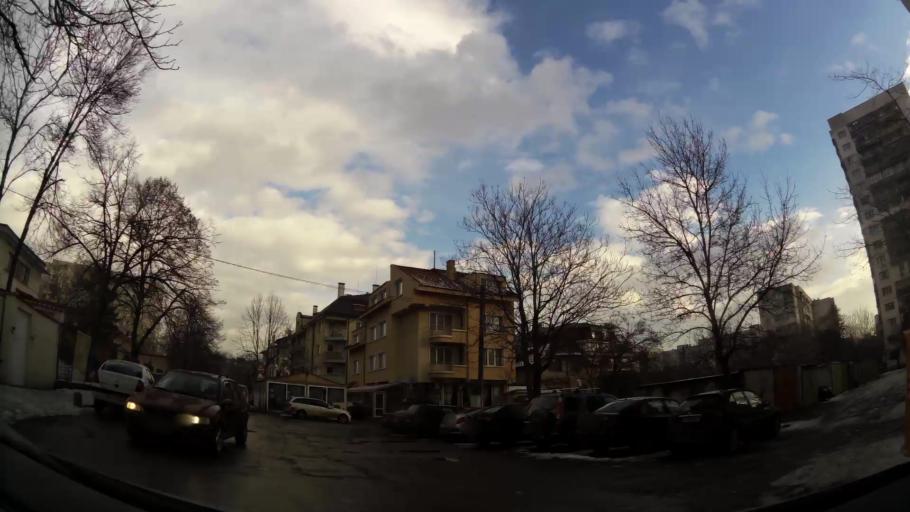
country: BG
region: Sofia-Capital
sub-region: Stolichna Obshtina
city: Sofia
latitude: 42.6979
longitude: 23.2812
